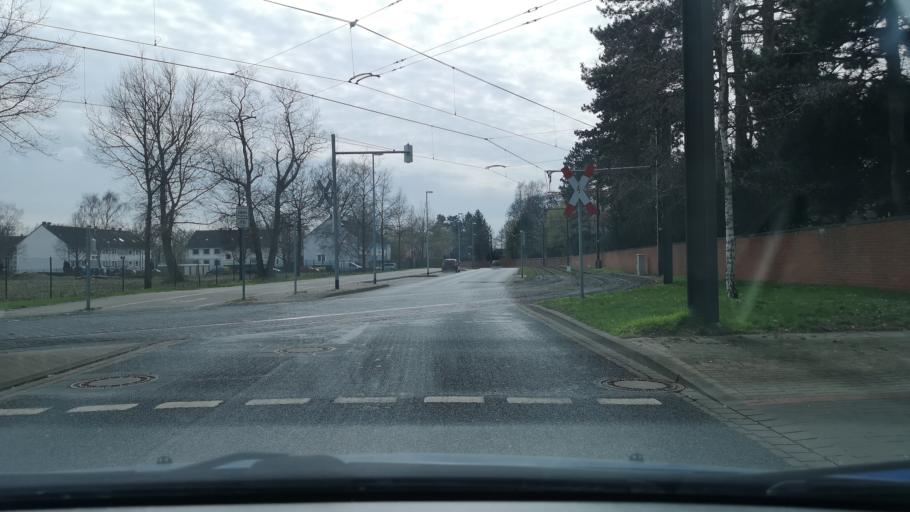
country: DE
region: Lower Saxony
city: Hannover
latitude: 52.4038
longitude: 9.6718
